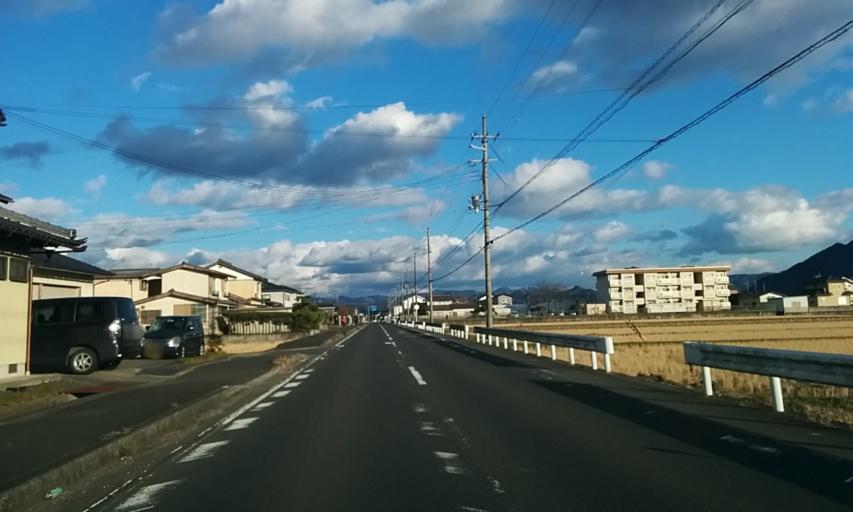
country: JP
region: Kyoto
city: Ayabe
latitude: 35.3118
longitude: 135.2133
